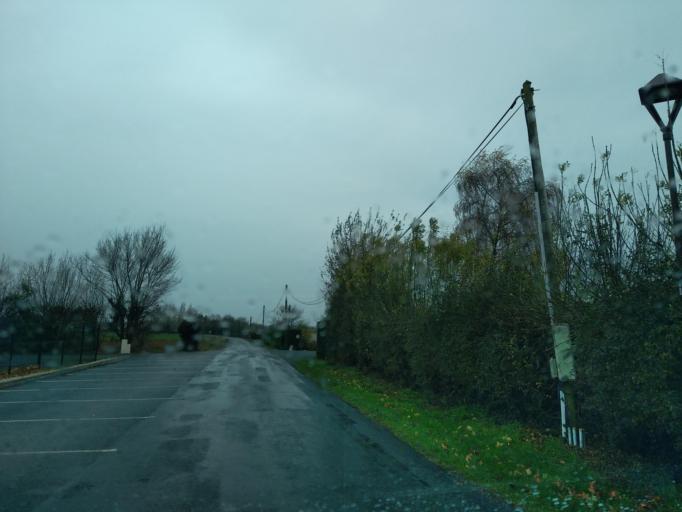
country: FR
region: Pays de la Loire
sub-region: Departement de la Vendee
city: Maillezais
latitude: 46.3695
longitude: -0.7352
